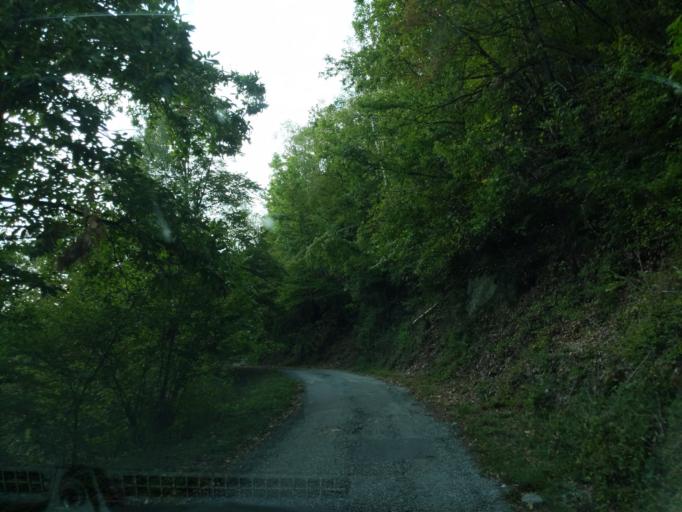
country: FR
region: Rhone-Alpes
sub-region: Departement de la Savoie
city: Aiton
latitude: 45.5195
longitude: 6.3327
